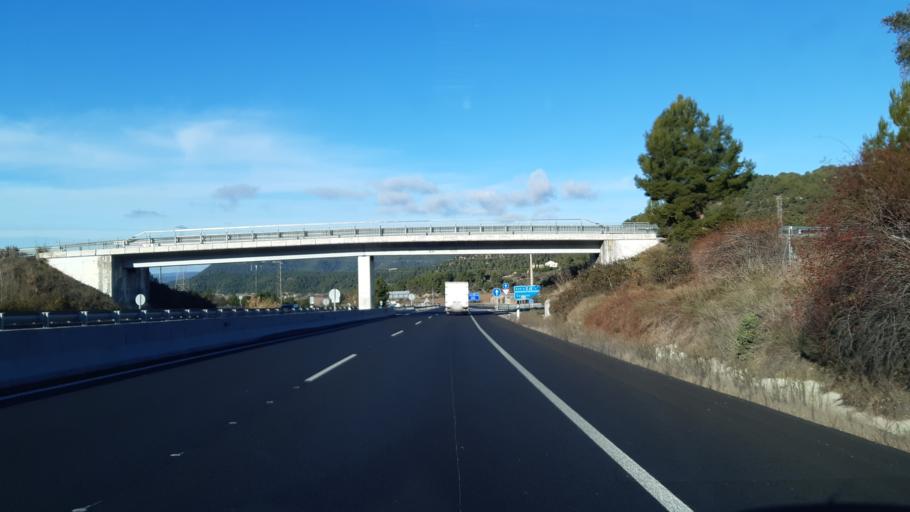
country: ES
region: Catalonia
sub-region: Provincia de Barcelona
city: Castelloli
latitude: 41.5952
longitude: 1.7212
